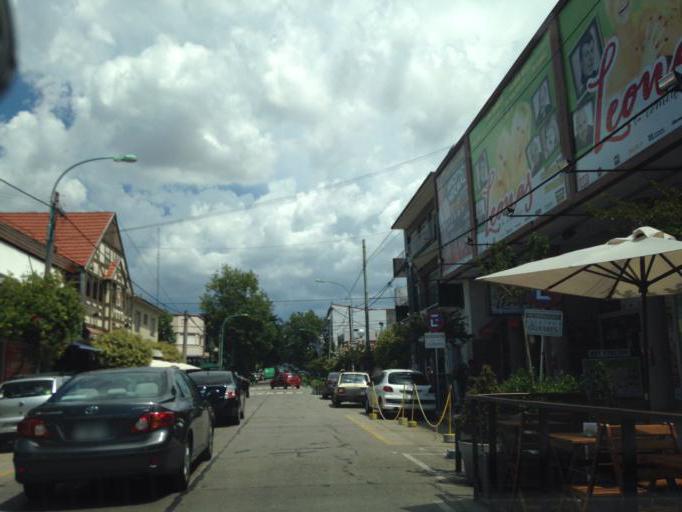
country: AR
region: Buenos Aires
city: Mar del Plata
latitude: -38.0160
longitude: -57.5419
